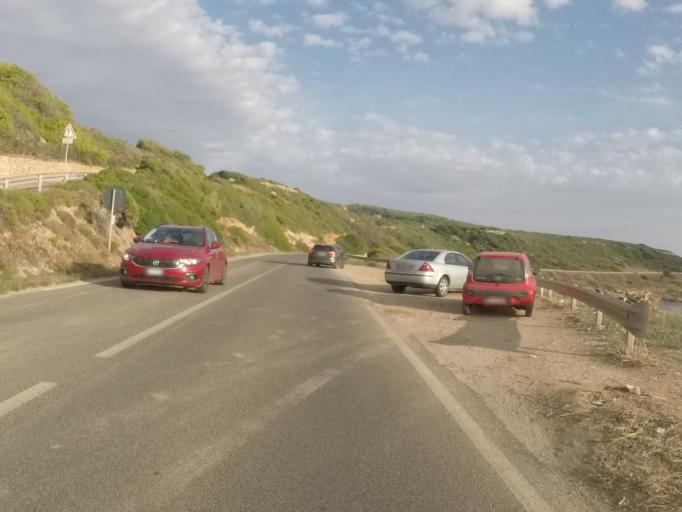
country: IT
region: Sardinia
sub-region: Provincia di Sassari
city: Alghero
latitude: 40.5414
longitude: 8.3223
